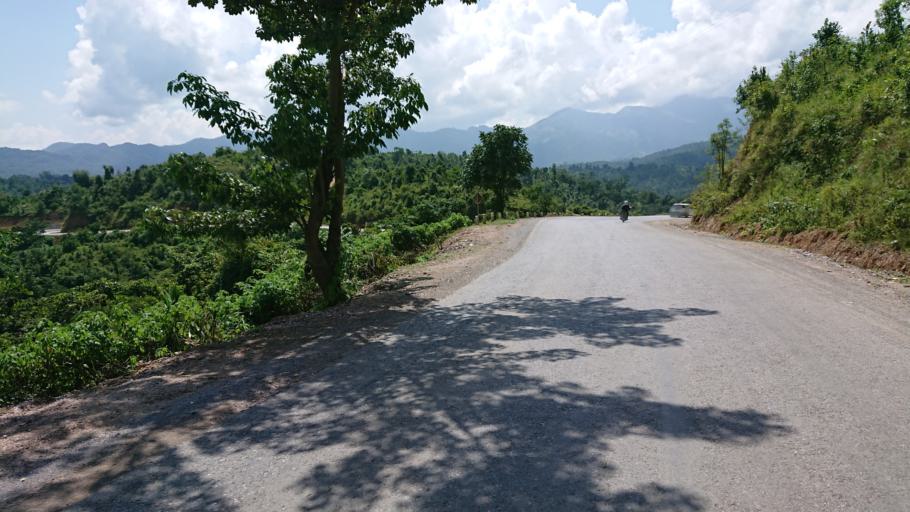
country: MM
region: Shan
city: Taunggyi
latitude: 20.8170
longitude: 97.3075
